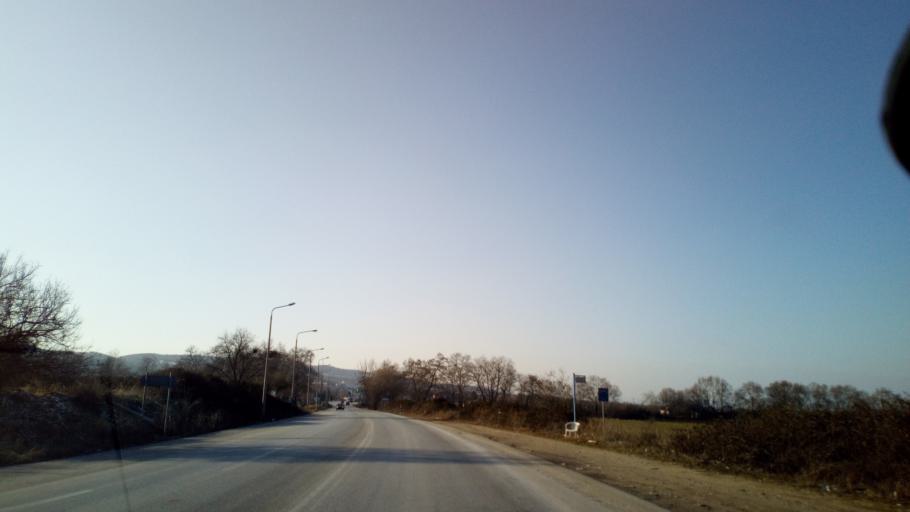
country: GR
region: Central Macedonia
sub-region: Nomos Thessalonikis
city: Gerakarou
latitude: 40.6346
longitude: 23.1967
